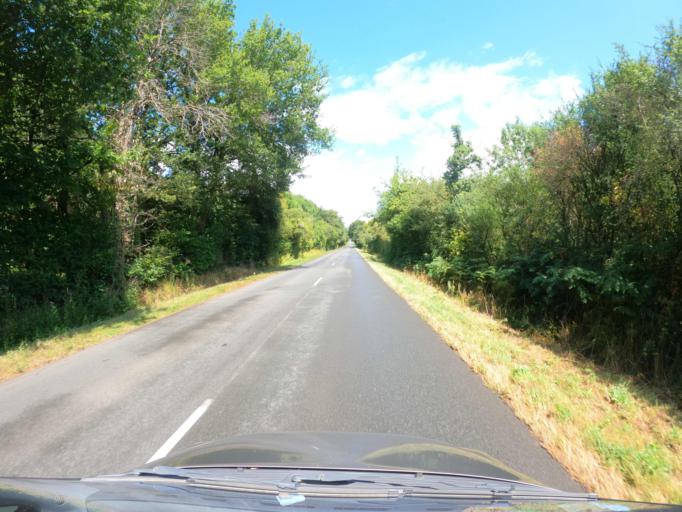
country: FR
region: Pays de la Loire
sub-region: Departement de Maine-et-Loire
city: Champigne
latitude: 47.6343
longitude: -0.5800
